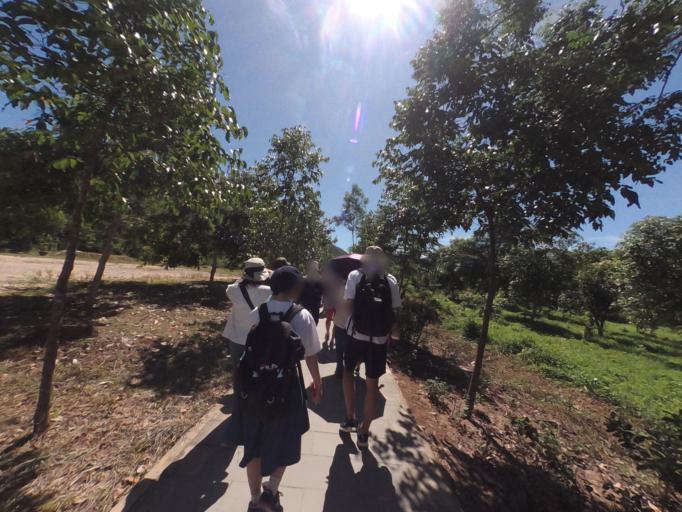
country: VN
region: Quang Nam
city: Dai Loc
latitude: 15.7682
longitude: 108.1196
